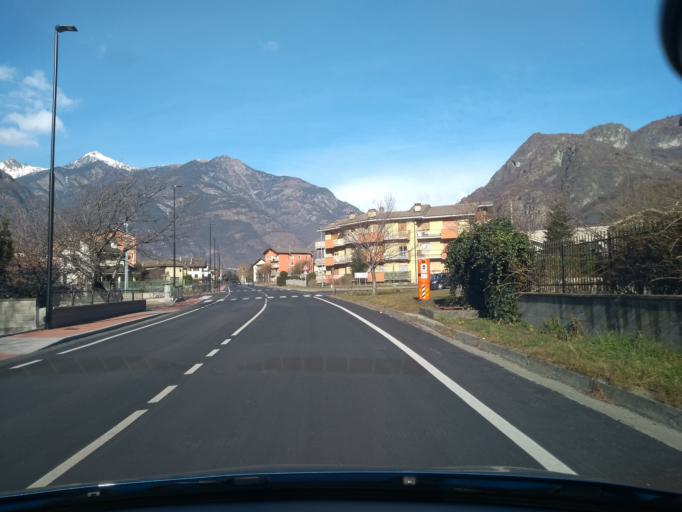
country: IT
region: Aosta Valley
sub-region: Valle d'Aosta
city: Verres
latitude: 45.6612
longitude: 7.6935
